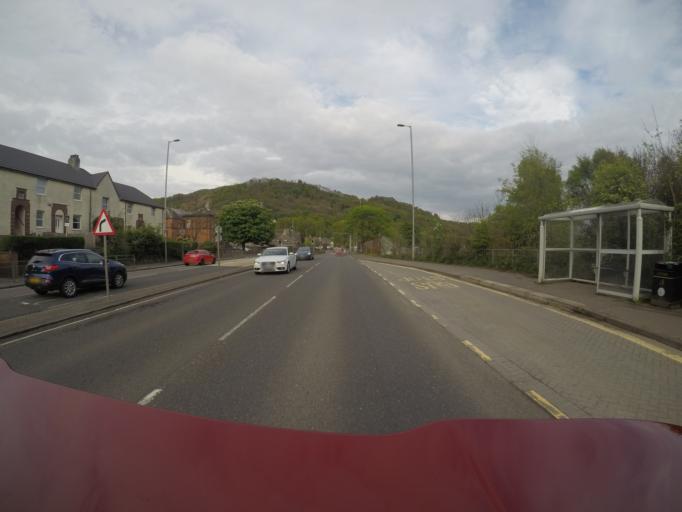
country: GB
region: Scotland
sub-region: Renfrewshire
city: Bishopton
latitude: 55.9358
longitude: -4.5217
